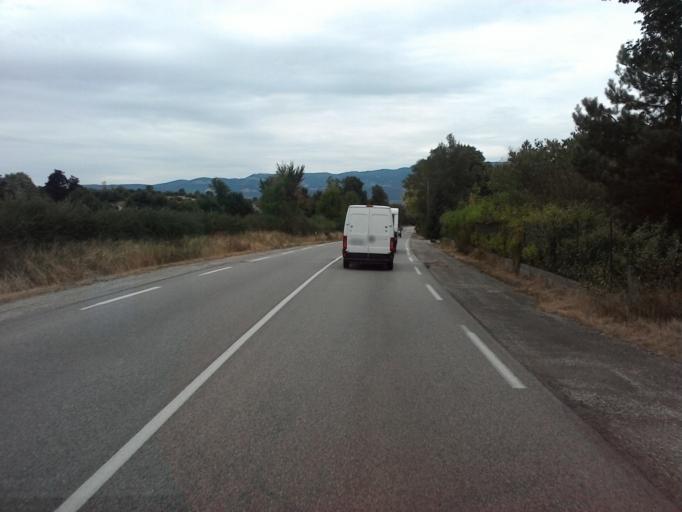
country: FR
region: Rhone-Alpes
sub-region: Departement de l'Isere
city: Bouvesse-Quirieu
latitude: 45.7899
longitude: 5.4007
